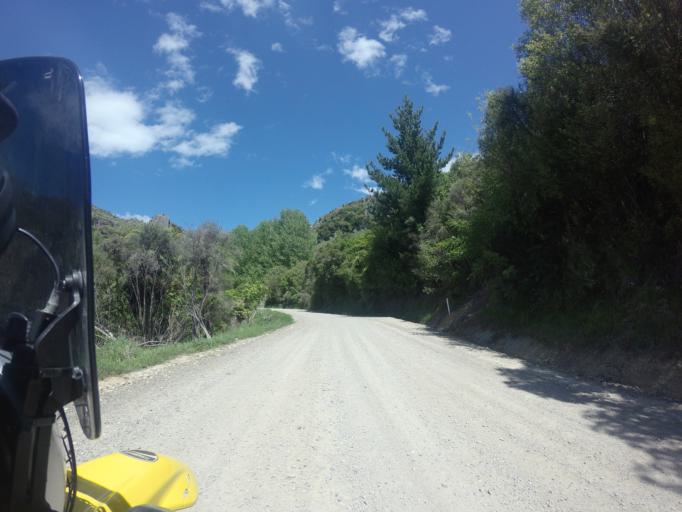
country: NZ
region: Hawke's Bay
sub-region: Wairoa District
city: Wairoa
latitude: -38.9907
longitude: 177.7166
